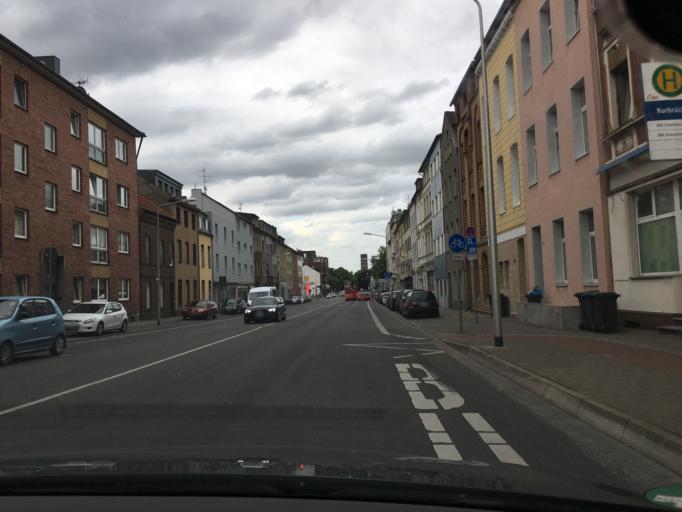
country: DE
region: North Rhine-Westphalia
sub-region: Regierungsbezirk Koln
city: Dueren
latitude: 50.7961
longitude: 6.4750
